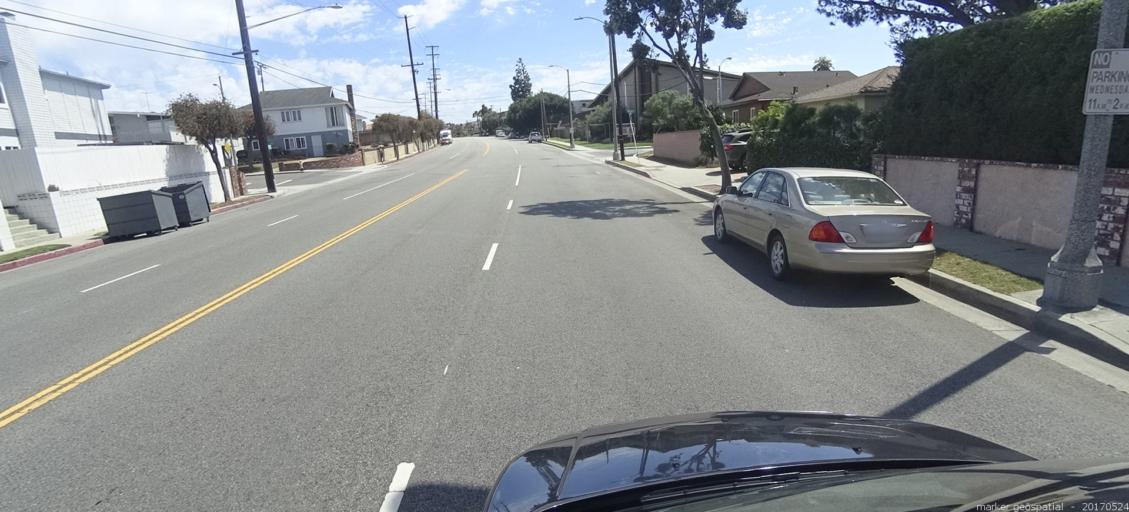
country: US
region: California
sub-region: Los Angeles County
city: Redondo Beach
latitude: 33.8374
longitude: -118.3765
